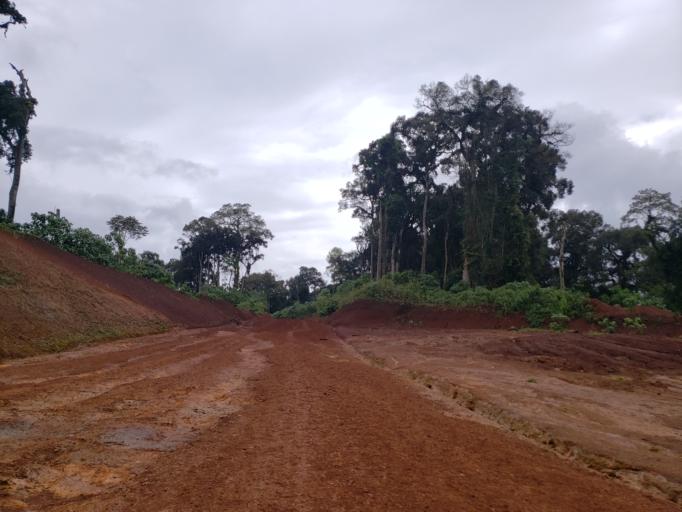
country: ET
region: Oromiya
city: Dodola
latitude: 6.5776
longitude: 39.4192
